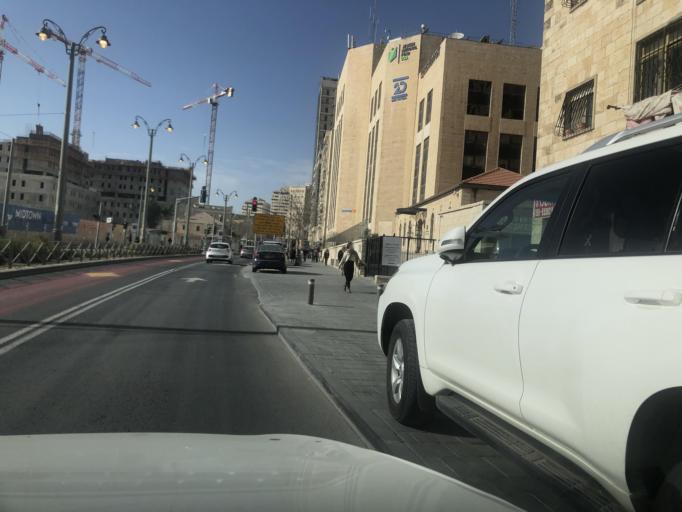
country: IL
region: Jerusalem
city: West Jerusalem
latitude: 31.7873
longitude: 35.2081
